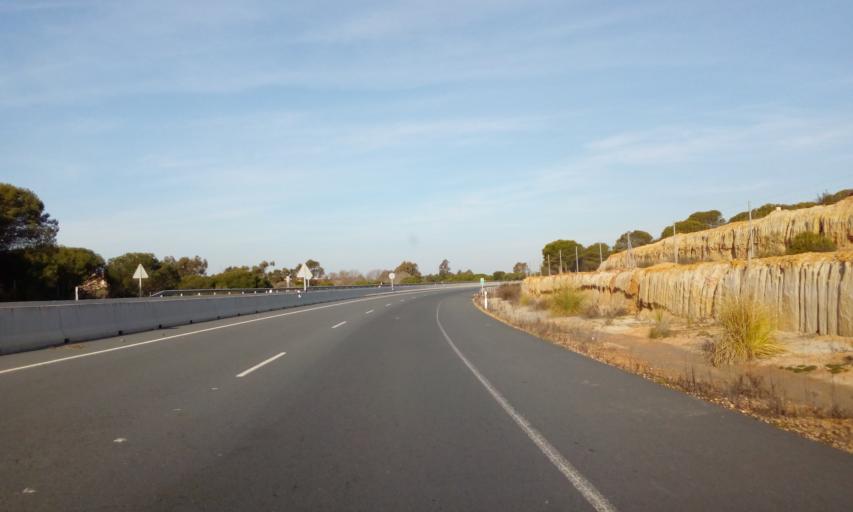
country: ES
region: Andalusia
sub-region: Provincia de Huelva
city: Lepe
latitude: 37.2143
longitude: -7.2195
